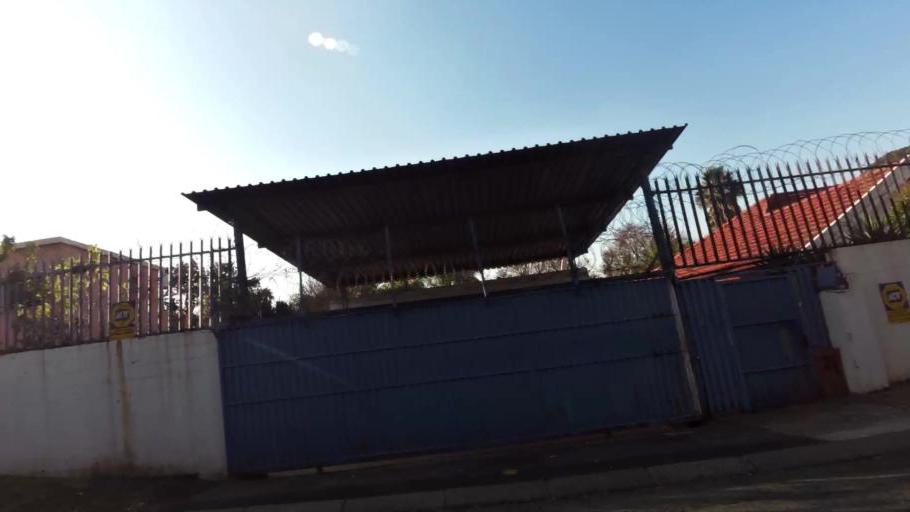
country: ZA
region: Gauteng
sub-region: City of Johannesburg Metropolitan Municipality
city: Johannesburg
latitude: -26.1873
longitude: 28.0032
